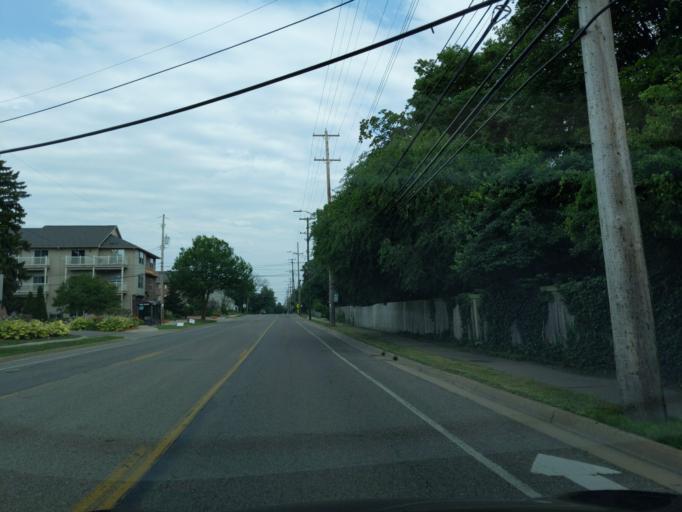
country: US
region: Michigan
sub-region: Ingham County
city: East Lansing
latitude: 42.7407
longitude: -84.4739
